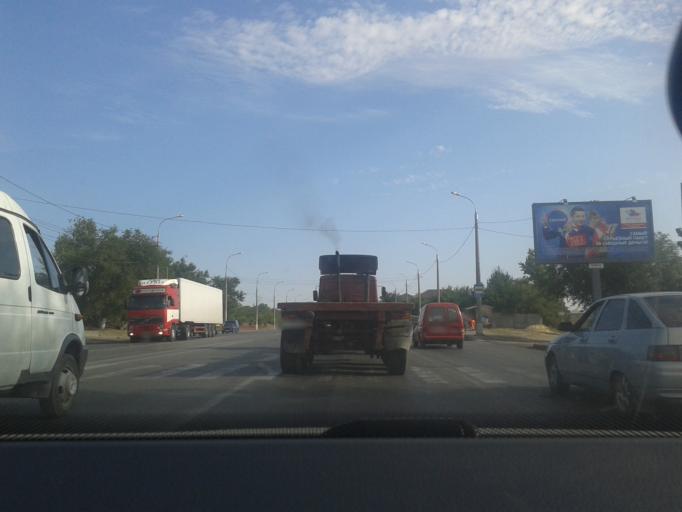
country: RU
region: Volgograd
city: Volgograd
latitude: 48.6706
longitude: 44.4424
